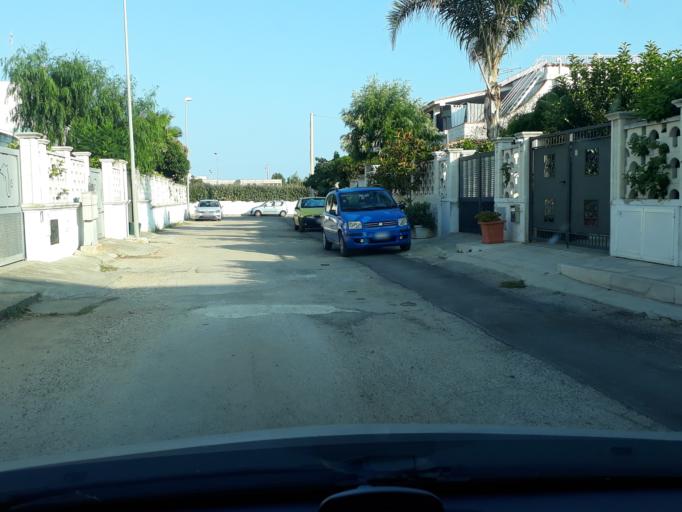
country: IT
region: Apulia
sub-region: Provincia di Brindisi
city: Carovigno
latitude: 40.7613
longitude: 17.6894
